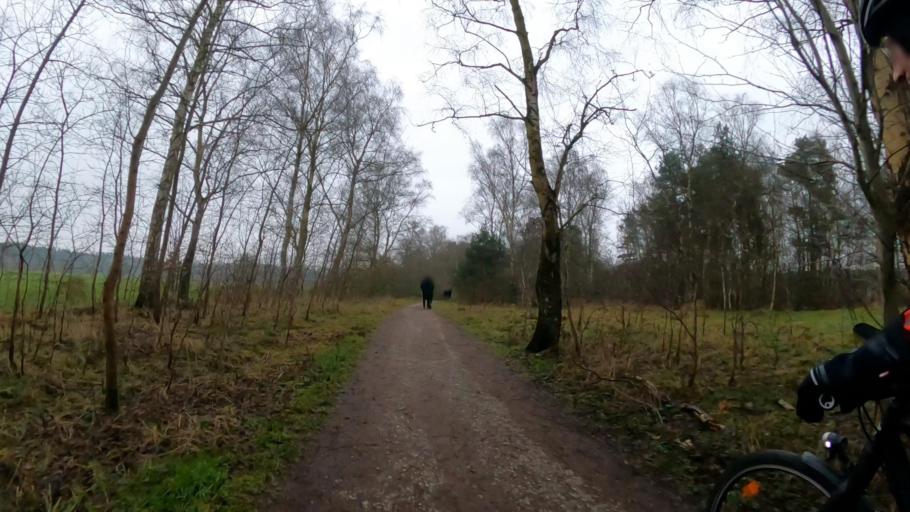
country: DE
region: Schleswig-Holstein
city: Appen
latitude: 53.6007
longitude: 9.7548
